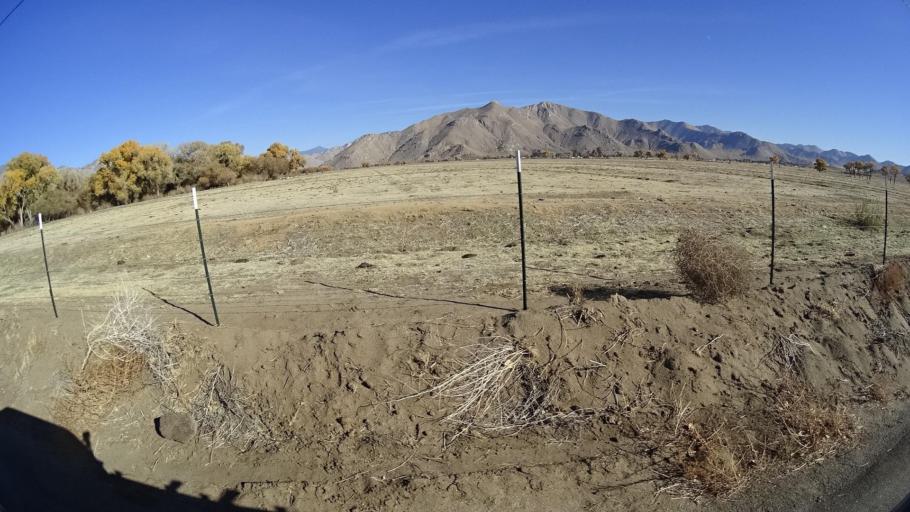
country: US
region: California
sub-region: Kern County
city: Weldon
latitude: 35.6697
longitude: -118.2903
